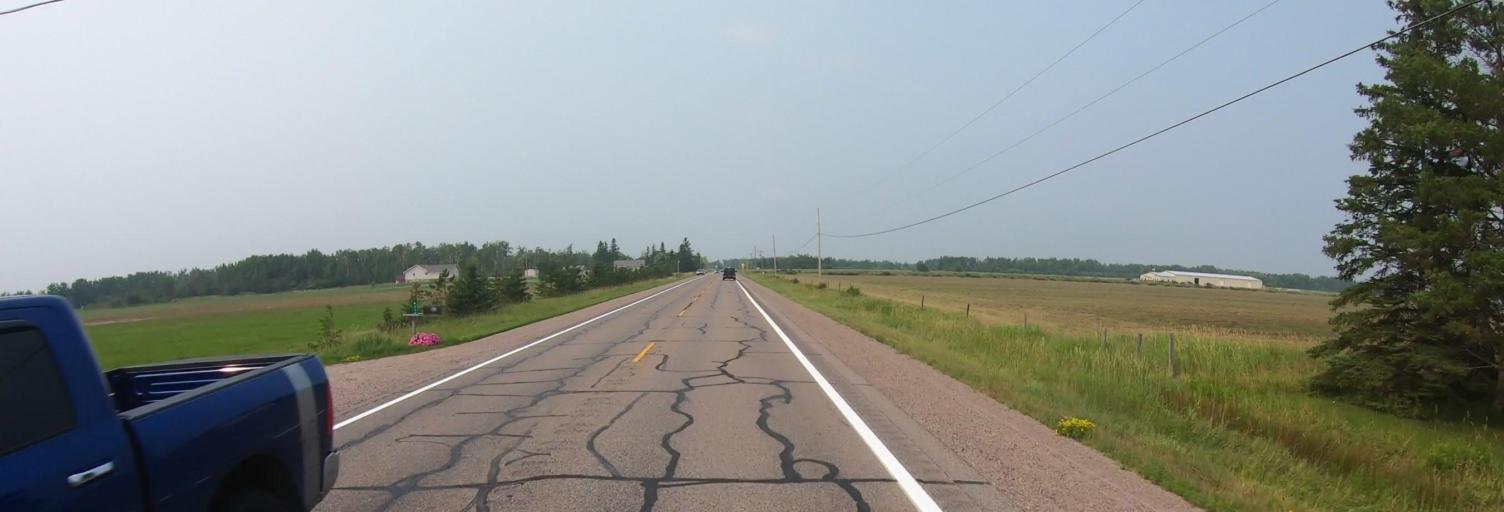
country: US
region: Michigan
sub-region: Chippewa County
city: Sault Ste. Marie
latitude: 46.4422
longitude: -84.3536
